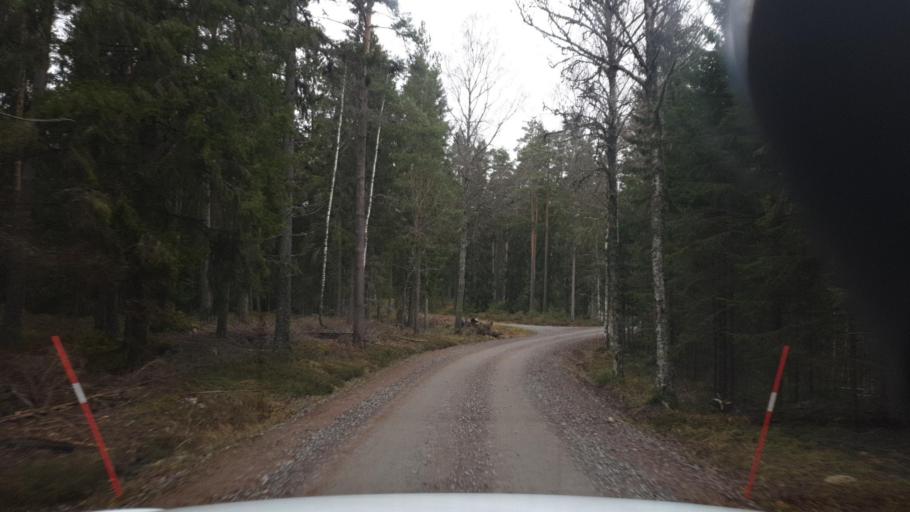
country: SE
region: Vaermland
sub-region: Karlstads Kommun
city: Edsvalla
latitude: 59.4608
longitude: 13.1009
